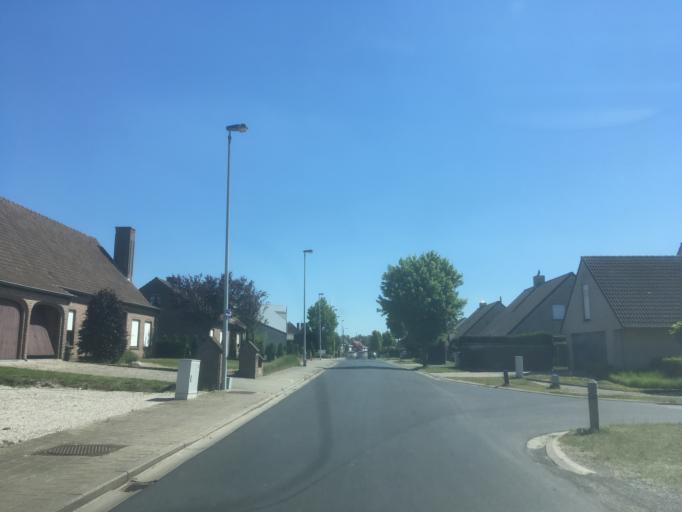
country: BE
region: Flanders
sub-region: Provincie West-Vlaanderen
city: Izegem
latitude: 50.9389
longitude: 3.1947
